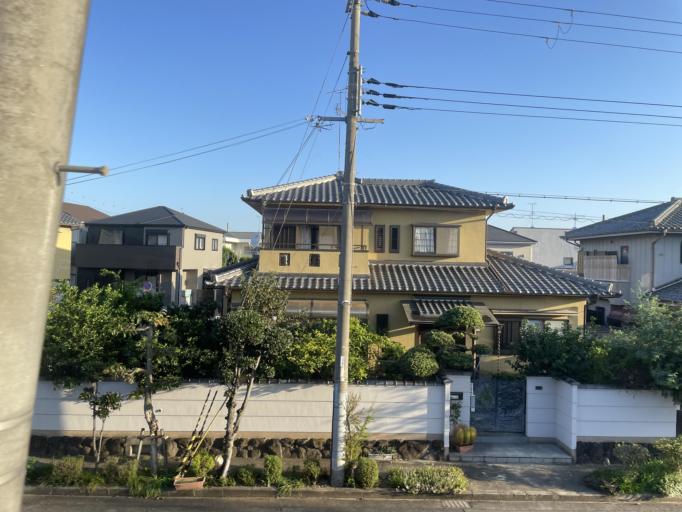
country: JP
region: Osaka
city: Kashihara
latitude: 34.5718
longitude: 135.5871
